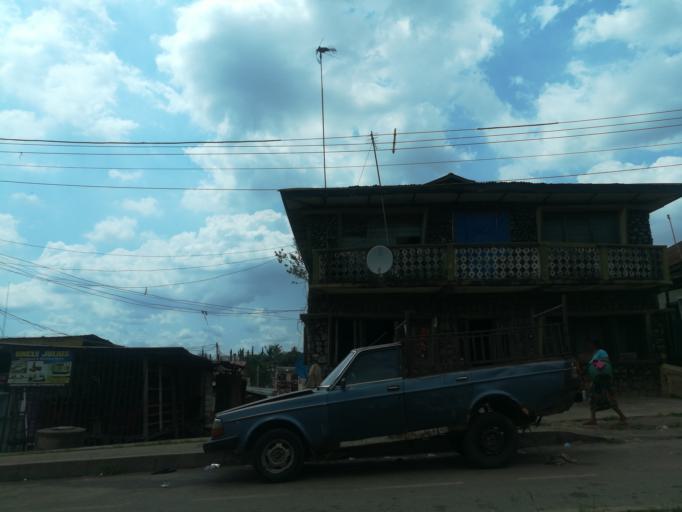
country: NG
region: Oyo
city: Ibadan
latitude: 7.3969
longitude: 3.8839
